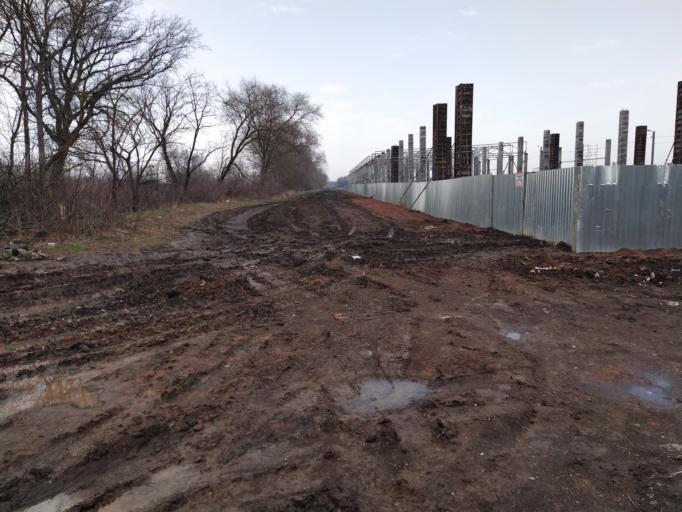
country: RU
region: Rostov
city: Bataysk
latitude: 47.1141
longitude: 39.7310
